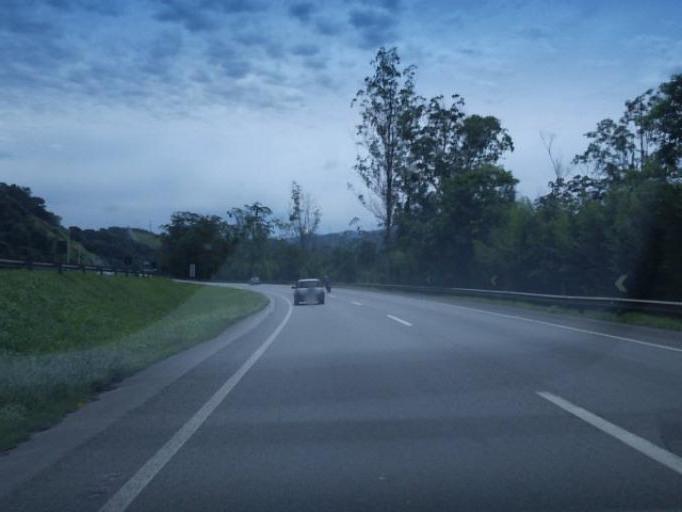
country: BR
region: Sao Paulo
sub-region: Miracatu
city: Miracatu
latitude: -24.1470
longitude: -47.3022
